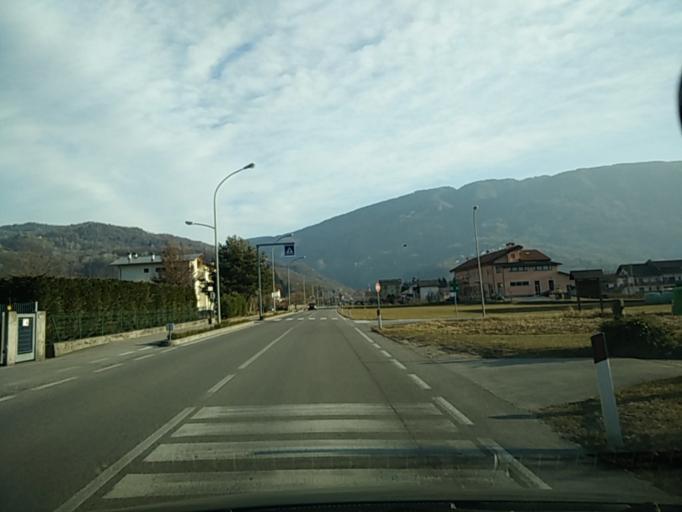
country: IT
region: Veneto
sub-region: Provincia di Belluno
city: Farra d'Alpago
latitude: 46.1294
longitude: 12.3476
